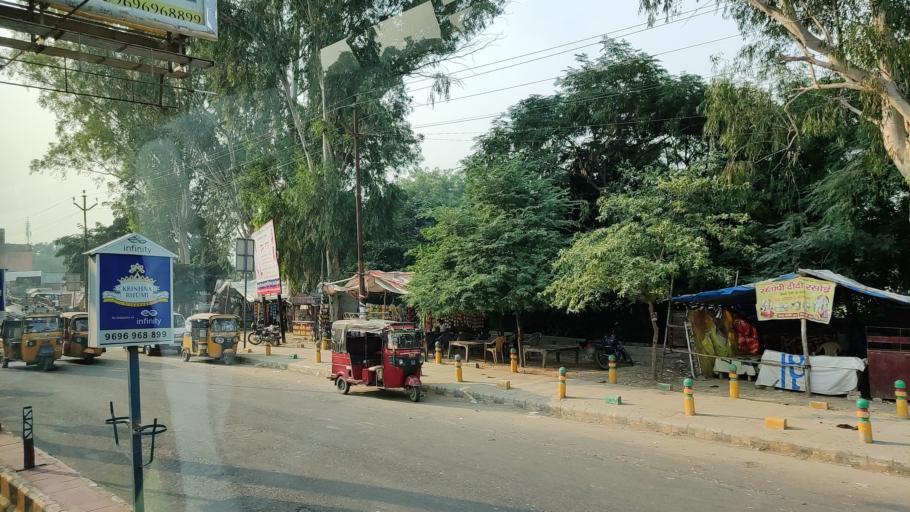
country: IN
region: Uttar Pradesh
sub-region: Mathura
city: Vrindavan
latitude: 27.5628
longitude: 77.6333
